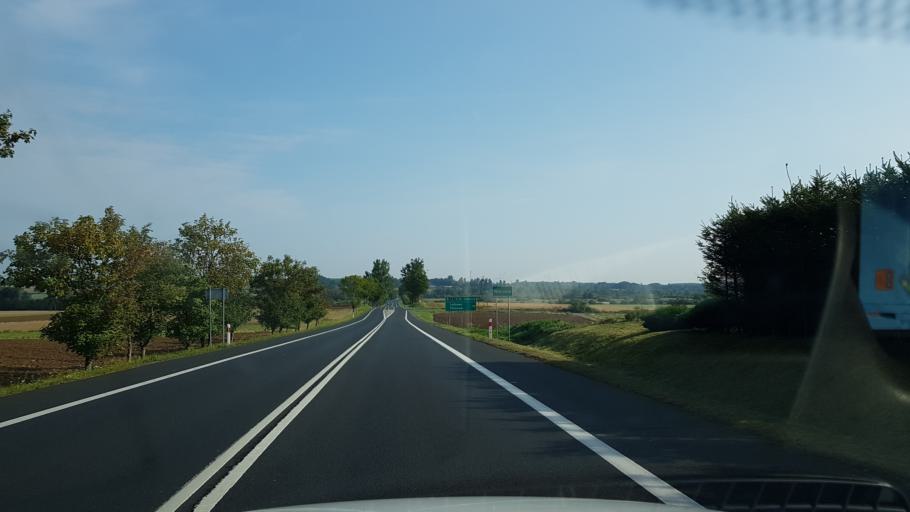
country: PL
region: West Pomeranian Voivodeship
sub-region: Powiat slawienski
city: Darlowo
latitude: 54.2817
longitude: 16.4866
